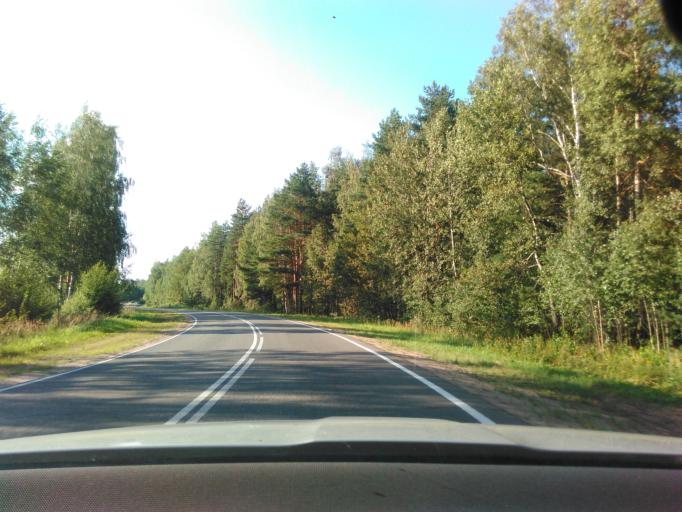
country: RU
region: Tverskaya
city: Zavidovo
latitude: 56.5924
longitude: 36.5418
